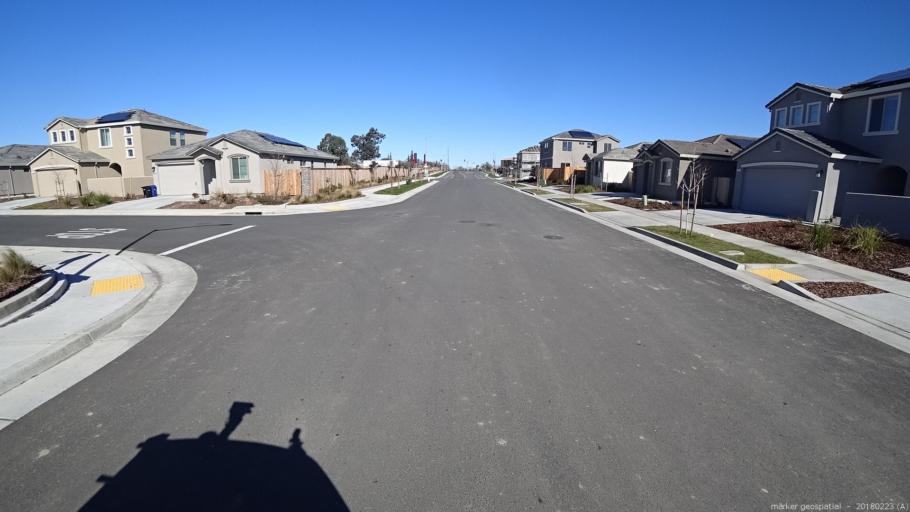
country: US
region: California
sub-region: Sacramento County
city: North Highlands
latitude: 38.7122
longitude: -121.3971
